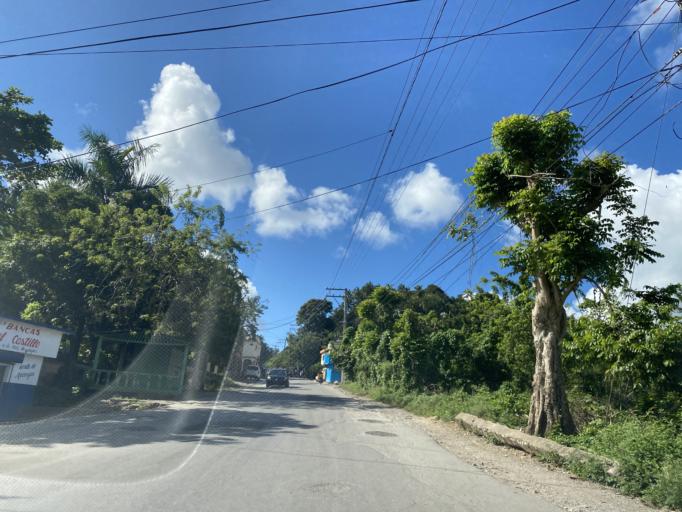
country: DO
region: Samana
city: Samana
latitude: 19.2069
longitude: -69.3494
